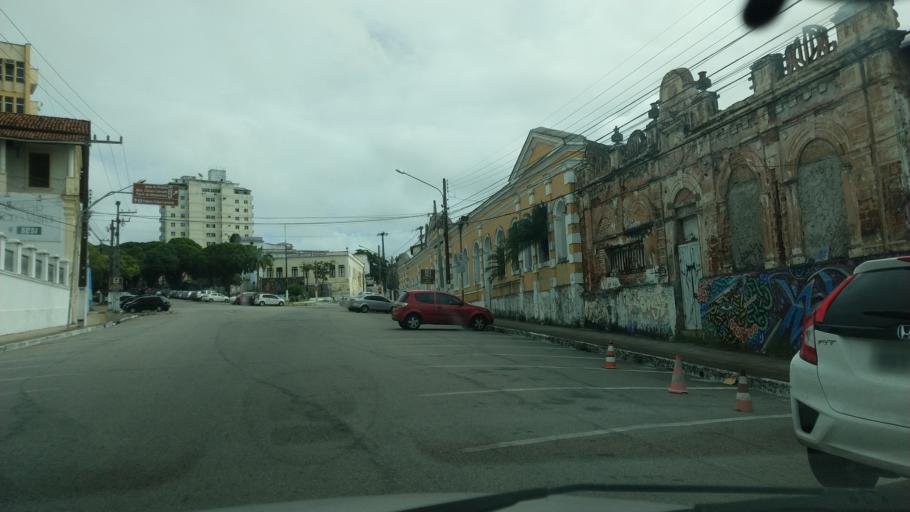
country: BR
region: Rio Grande do Norte
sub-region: Natal
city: Natal
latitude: -5.7821
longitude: -35.2067
